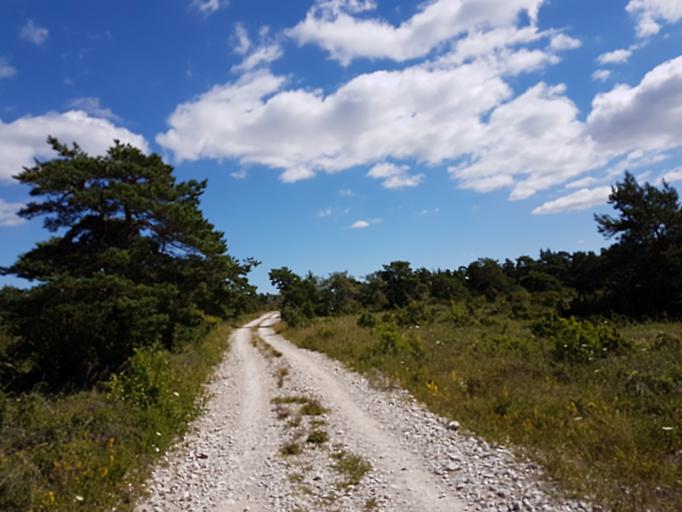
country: SE
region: Gotland
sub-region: Gotland
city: Visby
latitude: 57.6112
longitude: 18.3250
